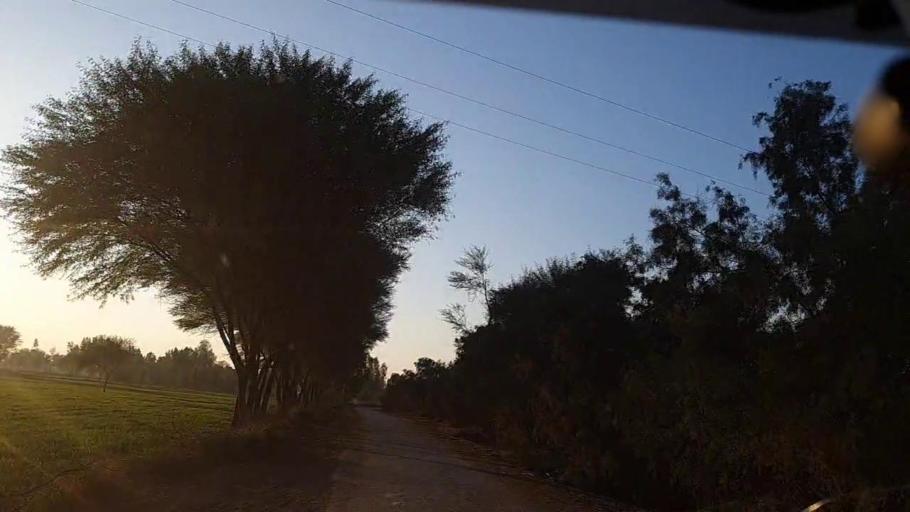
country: PK
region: Sindh
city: Khanpur
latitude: 27.8178
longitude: 69.3014
